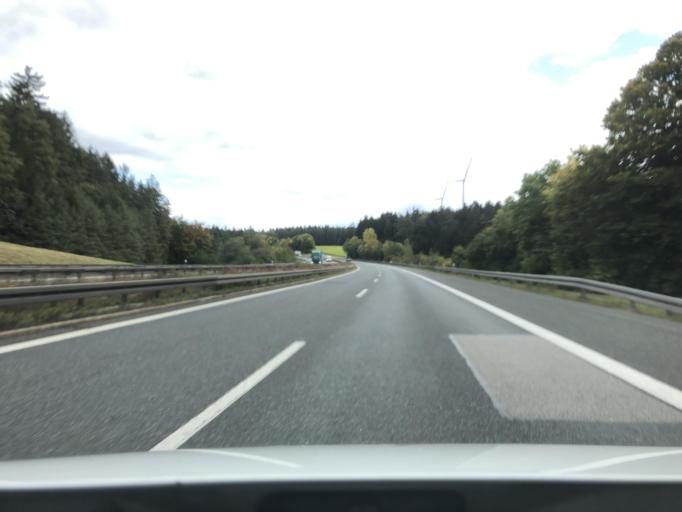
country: DE
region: Bavaria
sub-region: Upper Palatinate
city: Illschwang
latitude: 49.4207
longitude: 11.7118
